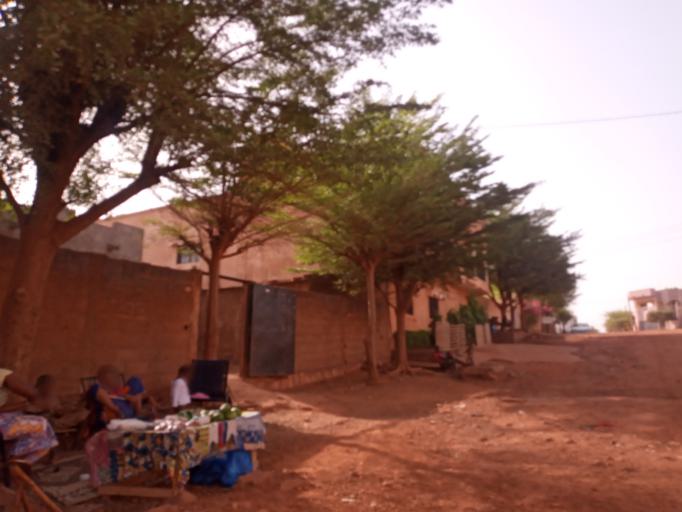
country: ML
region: Bamako
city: Bamako
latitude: 12.6854
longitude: -7.9384
